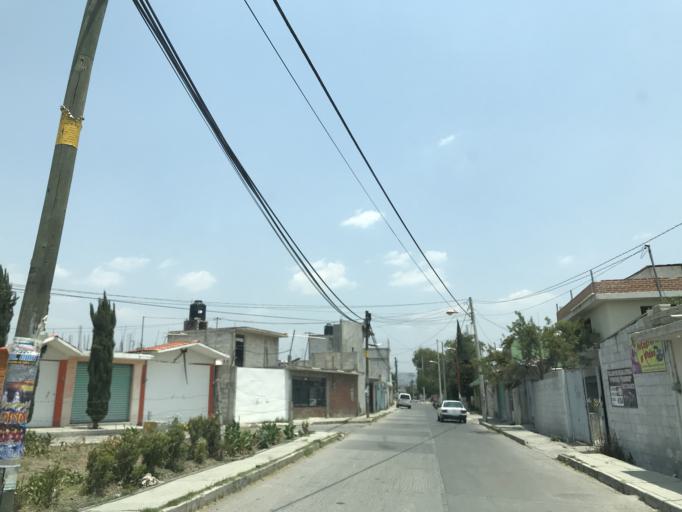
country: MX
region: Tlaxcala
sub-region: Ixtacuixtla de Mariano Matamoros
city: Santa Justina Ecatepec
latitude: 19.3091
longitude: -98.3721
